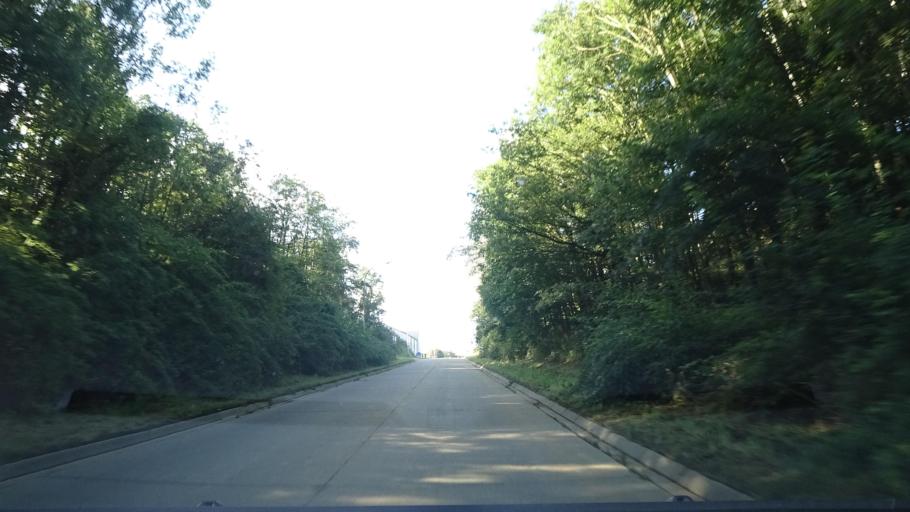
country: BE
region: Wallonia
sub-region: Province du Brabant Wallon
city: Villers-la-Ville
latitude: 50.6211
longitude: 4.5118
